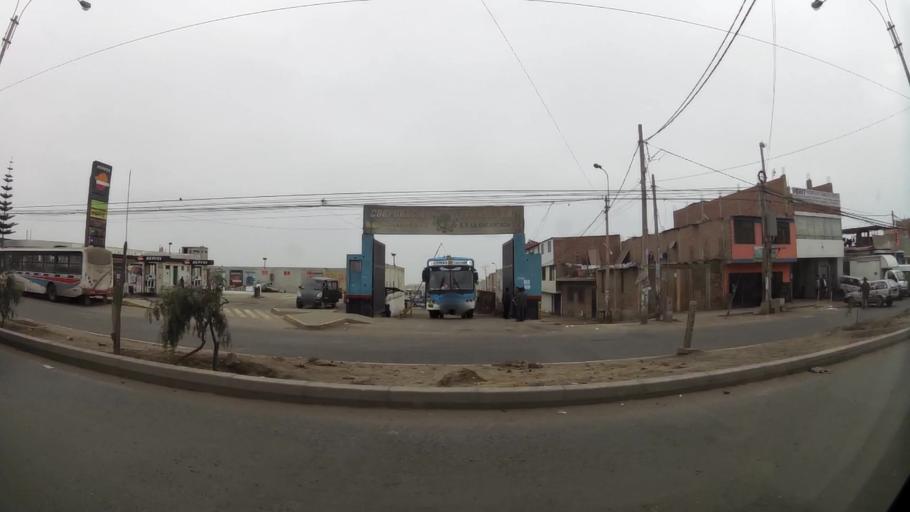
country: PE
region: Lima
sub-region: Lima
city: Punta Hermosa
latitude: -12.2408
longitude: -76.9143
